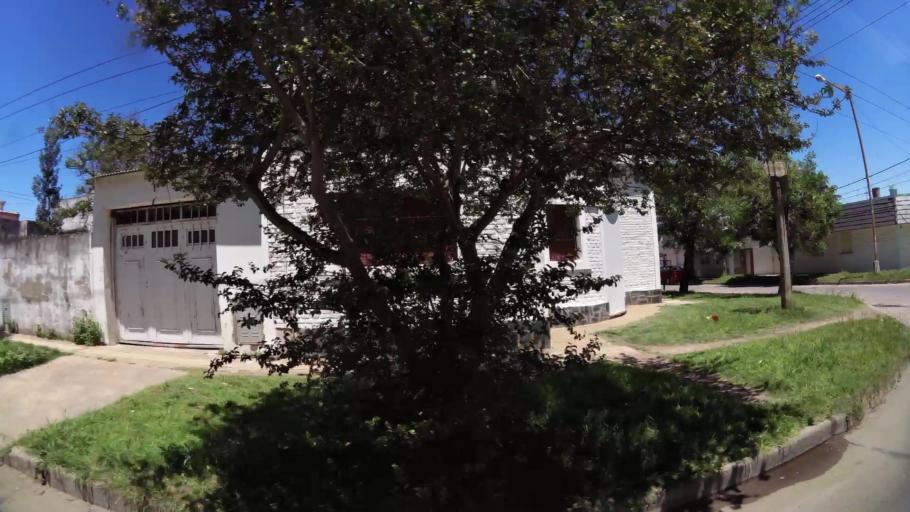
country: AR
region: Santa Fe
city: Santa Fe de la Vera Cruz
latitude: -31.6556
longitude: -60.7258
